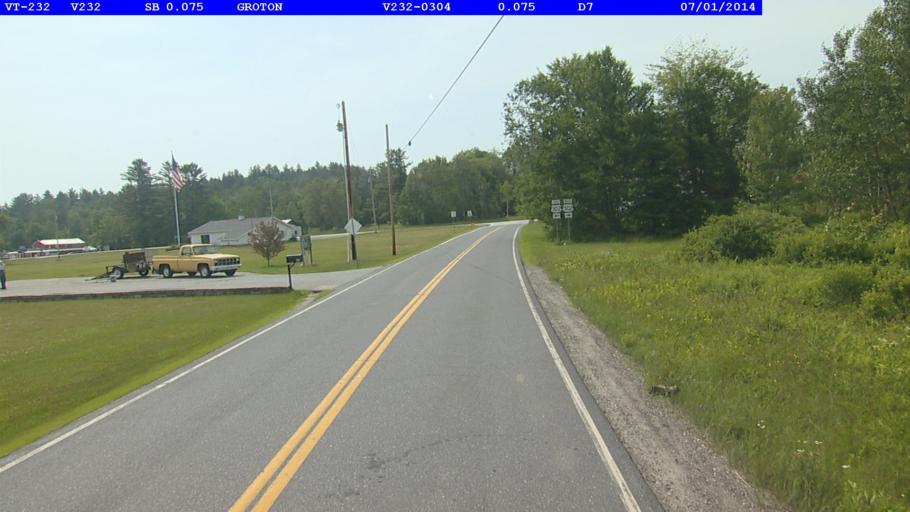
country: US
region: New Hampshire
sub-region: Grafton County
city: Woodsville
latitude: 44.2206
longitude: -72.2260
